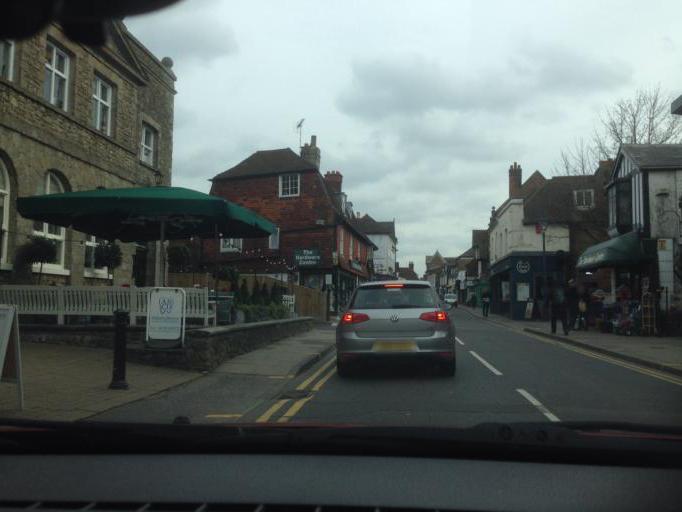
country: GB
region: England
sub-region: Kent
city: Sevenoaks
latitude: 51.2714
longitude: 0.1911
